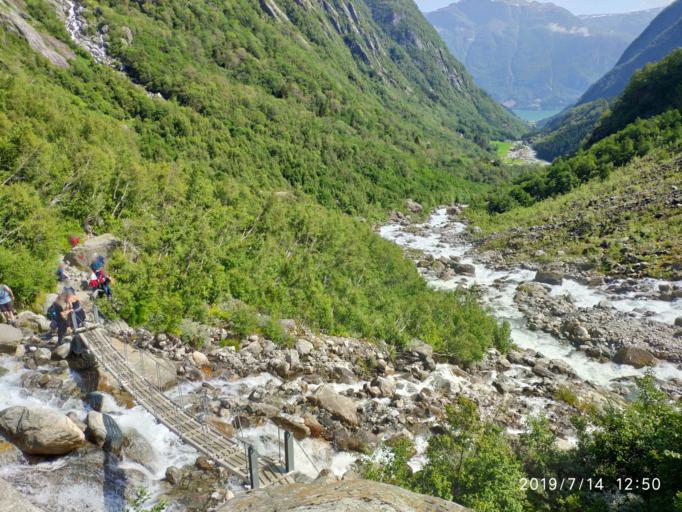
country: NO
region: Hordaland
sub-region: Odda
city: Odda
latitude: 60.0449
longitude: 6.4480
